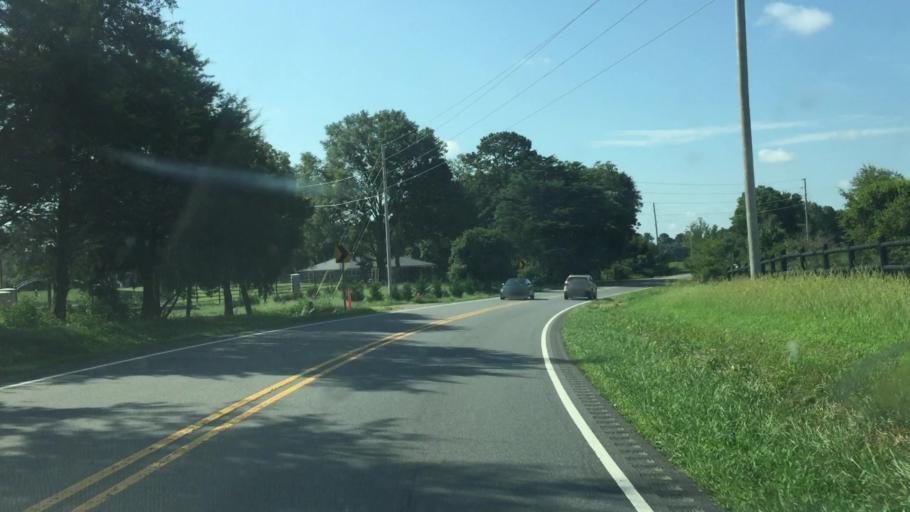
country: US
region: North Carolina
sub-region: Union County
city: Fairview
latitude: 35.1499
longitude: -80.5523
